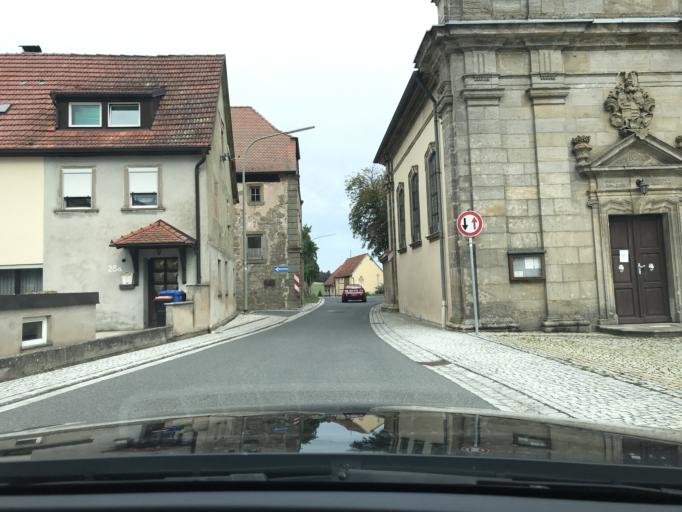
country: DE
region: Bavaria
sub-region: Regierungsbezirk Unterfranken
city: Burgpreppach
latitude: 50.1389
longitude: 10.6813
